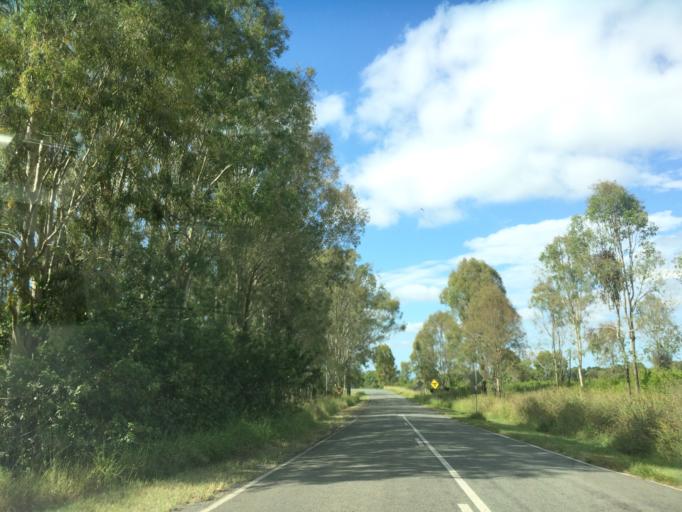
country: AU
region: Queensland
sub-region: Logan
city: Cedar Vale
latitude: -27.8892
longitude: 152.9735
